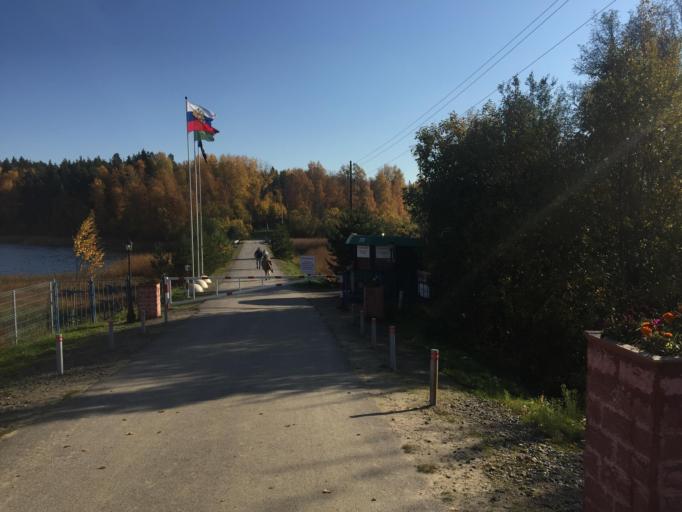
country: RU
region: Leningrad
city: Priozersk
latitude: 61.2865
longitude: 30.0888
